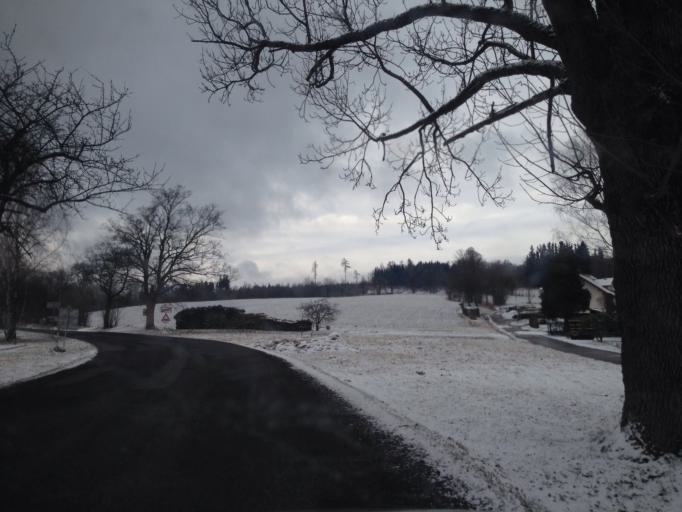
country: CZ
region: Liberecky
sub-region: Okres Semily
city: Vysoke nad Jizerou
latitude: 50.7032
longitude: 15.3860
